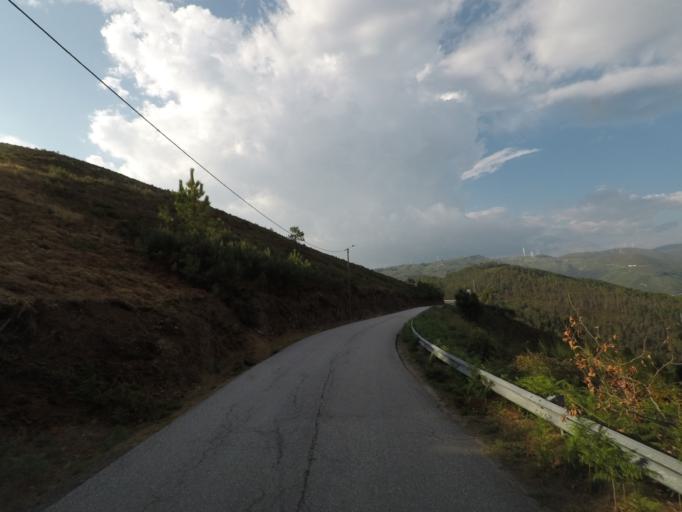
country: PT
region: Porto
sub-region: Baiao
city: Valadares
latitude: 41.1786
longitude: -7.9353
